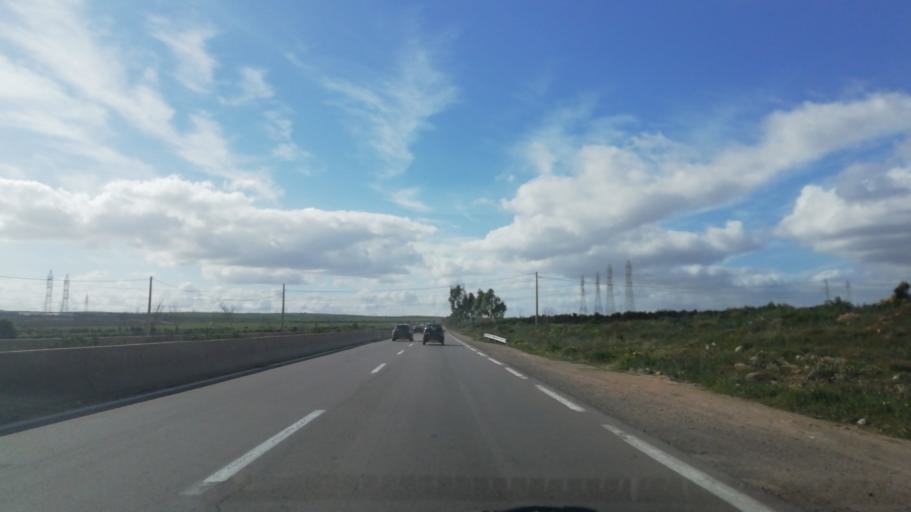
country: DZ
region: Oran
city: Ain el Bya
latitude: 35.7743
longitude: -0.1952
